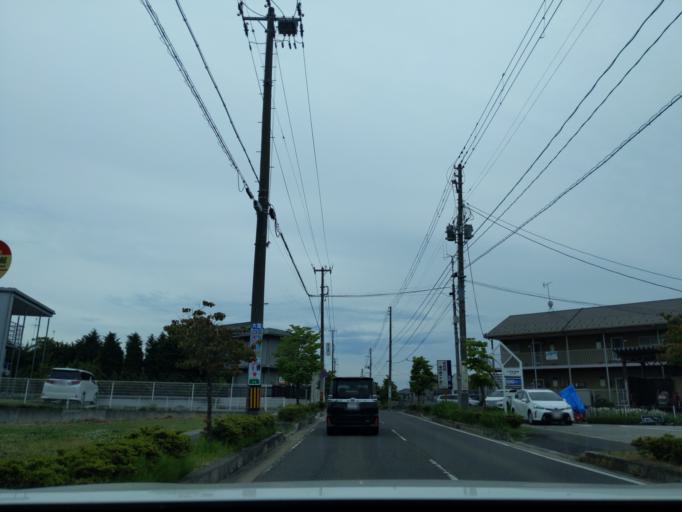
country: JP
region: Fukushima
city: Koriyama
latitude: 37.3739
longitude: 140.3652
